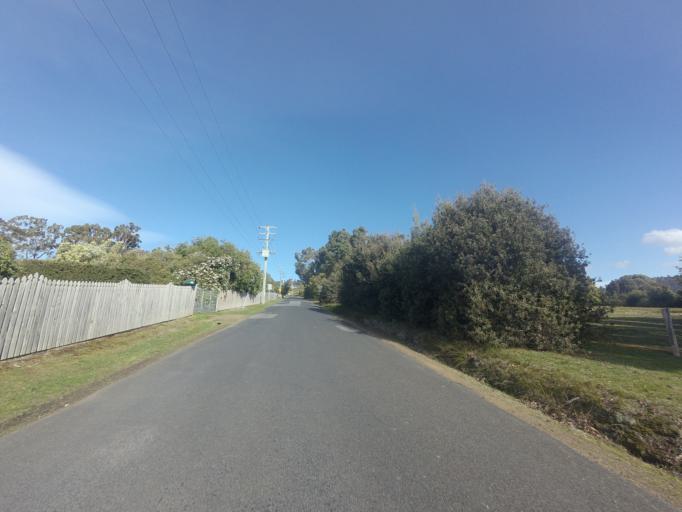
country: AU
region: Tasmania
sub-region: Kingborough
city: Margate
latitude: -43.0735
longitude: 147.2654
